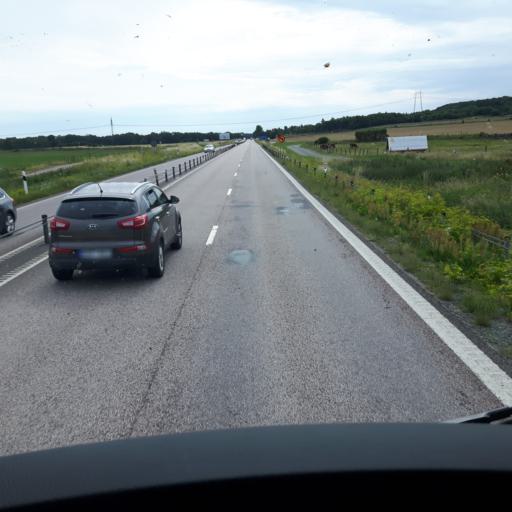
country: SE
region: Skane
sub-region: Hassleholms Kommun
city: Hassleholm
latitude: 56.1226
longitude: 13.8375
